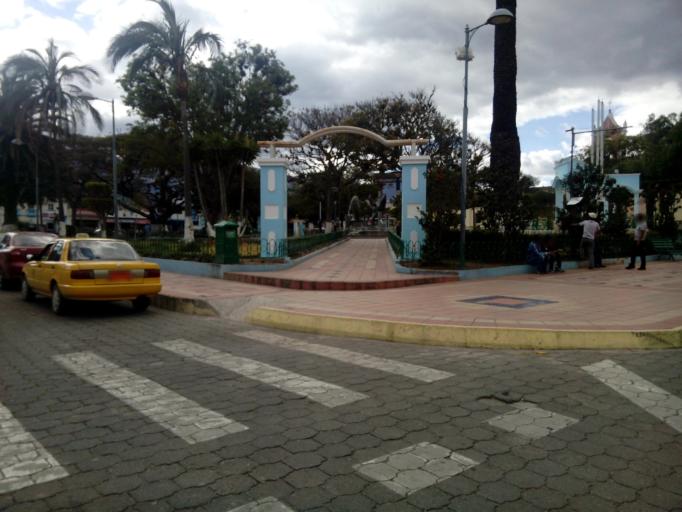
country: EC
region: Imbabura
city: Atuntaqui
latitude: 0.4169
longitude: -78.1938
